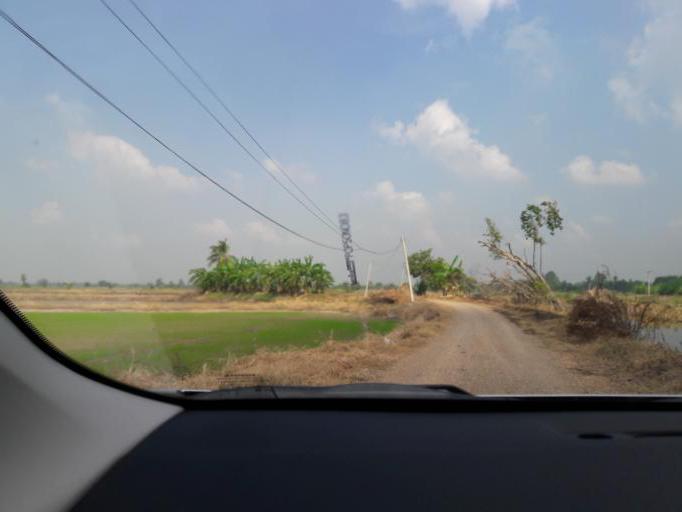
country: TH
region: Ang Thong
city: Ang Thong
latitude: 14.5649
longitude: 100.4094
